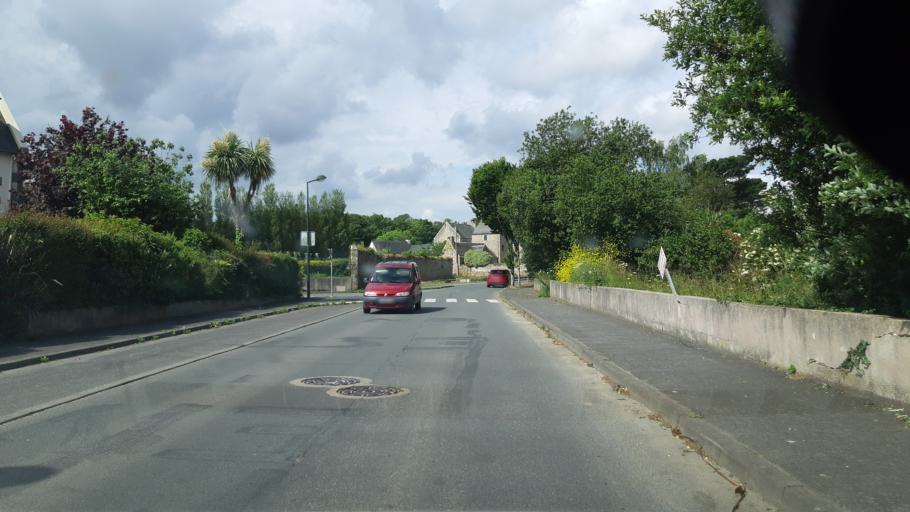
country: FR
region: Brittany
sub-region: Departement du Finistere
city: Saint-Pol-de-Leon
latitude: 48.6809
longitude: -3.9746
